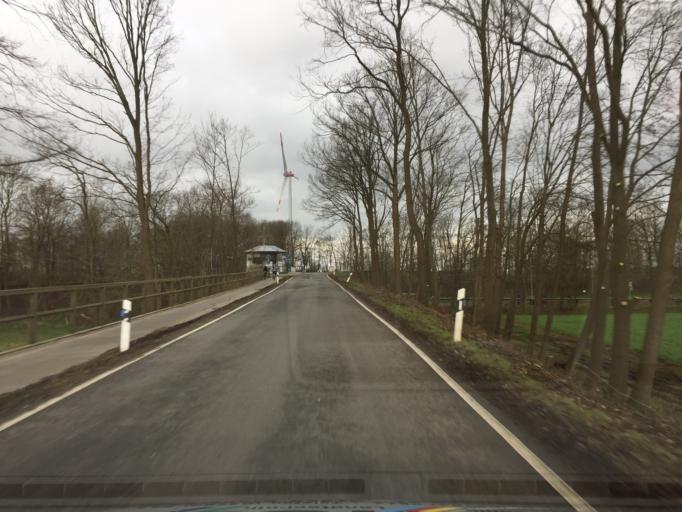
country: DE
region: Lower Saxony
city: Stolzenau
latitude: 52.4938
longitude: 9.0615
